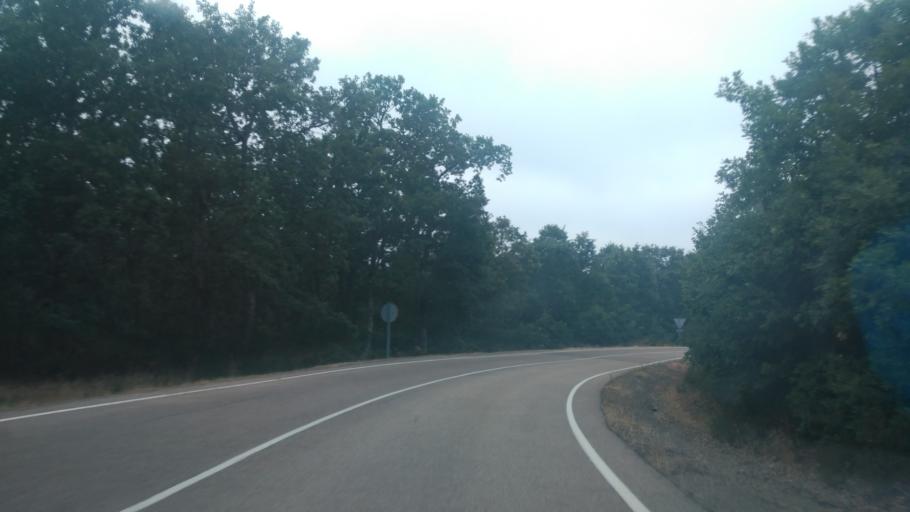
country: ES
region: Castille and Leon
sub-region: Provincia de Salamanca
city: Cilleros de la Bastida
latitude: 40.5565
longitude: -6.0684
